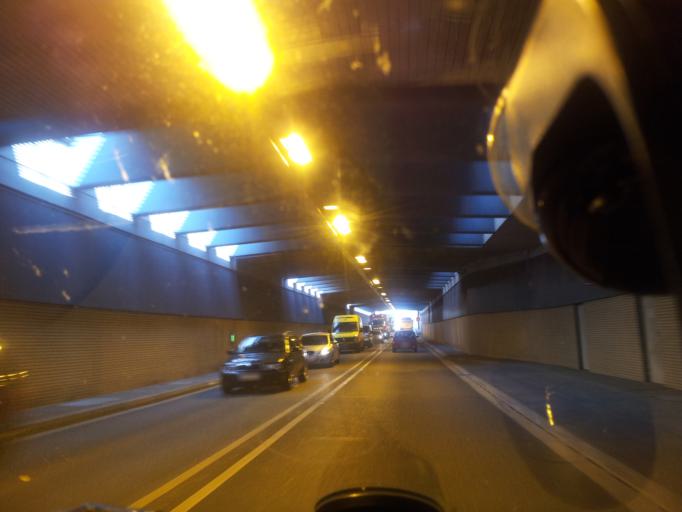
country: DE
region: Saxony-Anhalt
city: Neue Neustadt
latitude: 52.1390
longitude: 11.6396
